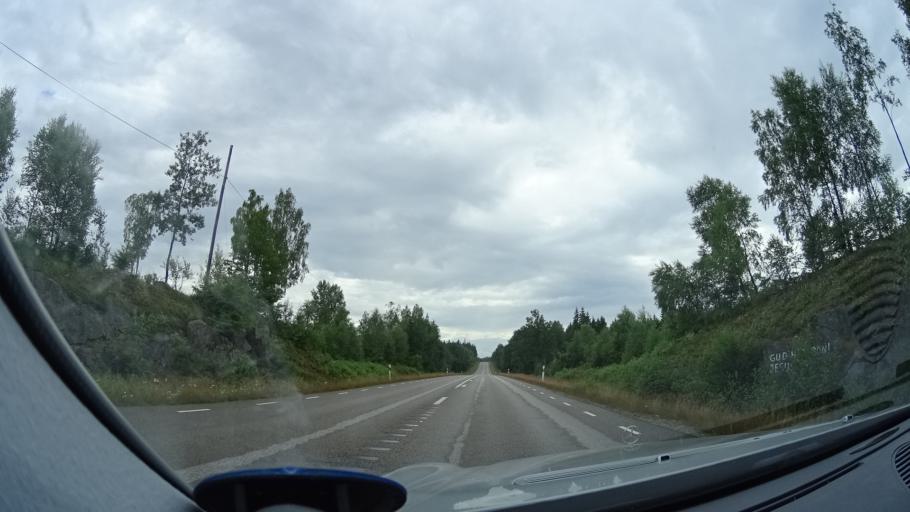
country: SE
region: Kronoberg
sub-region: Tingsryds Kommun
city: Tingsryd
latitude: 56.4519
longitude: 14.9922
